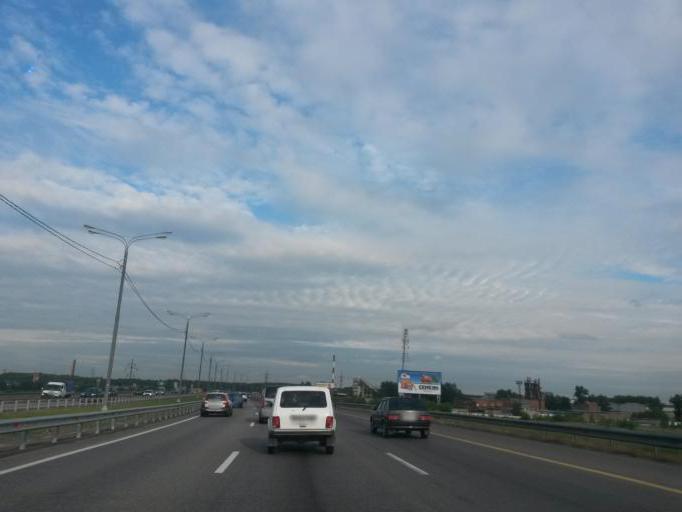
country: RU
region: Moskovskaya
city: Domodedovo
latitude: 55.4617
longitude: 37.7615
